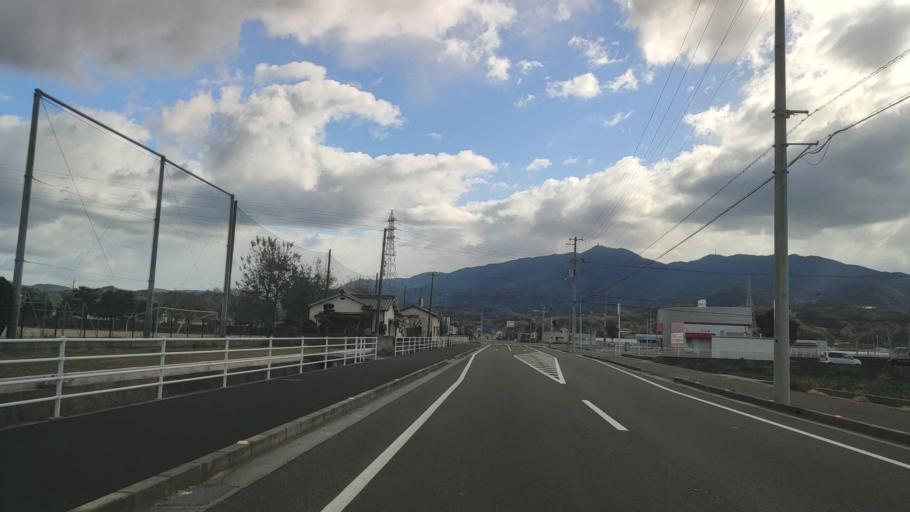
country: JP
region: Ehime
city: Hojo
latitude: 33.9701
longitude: 132.7815
